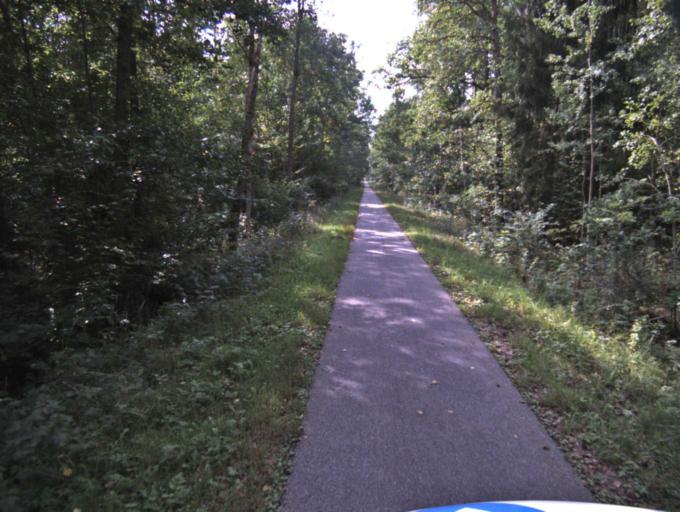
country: SE
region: Vaestra Goetaland
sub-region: Tranemo Kommun
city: Limmared
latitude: 57.6318
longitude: 13.3516
